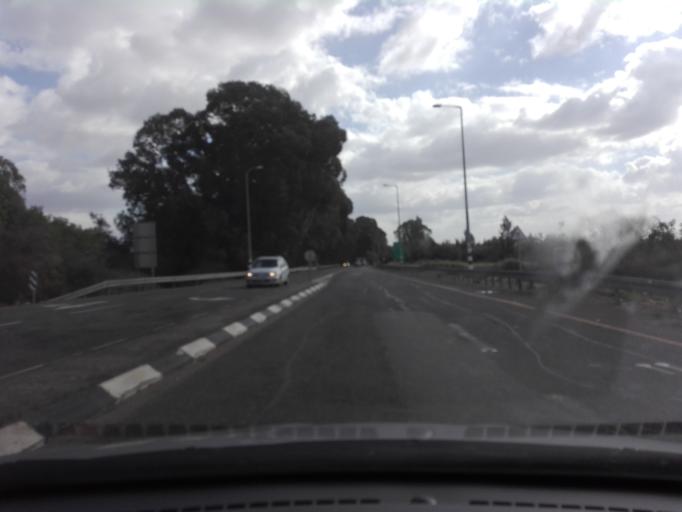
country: PS
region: West Bank
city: Nazlat `Isa
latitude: 32.4644
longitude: 34.9947
